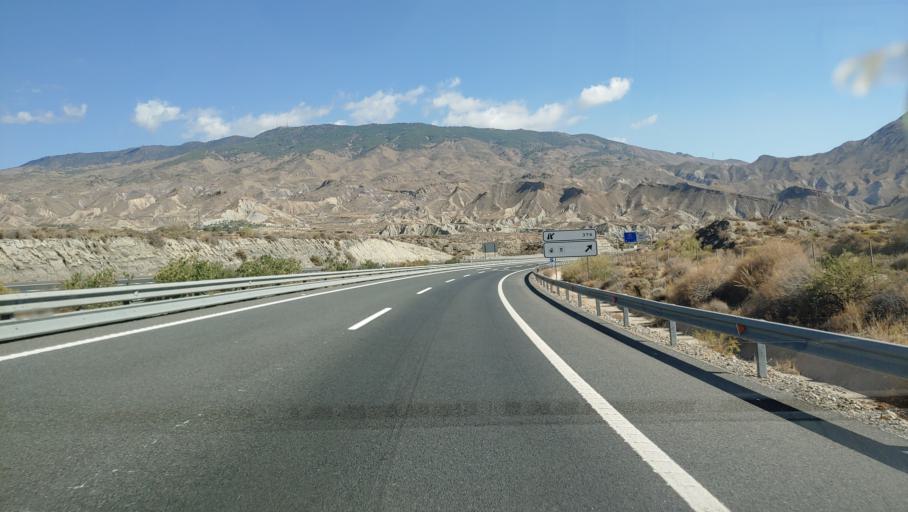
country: ES
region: Andalusia
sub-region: Provincia de Almeria
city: Tabernas
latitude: 37.0256
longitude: -2.4456
